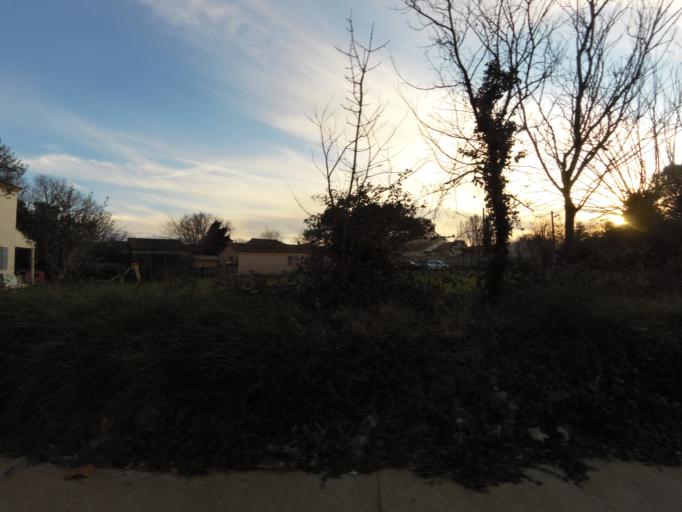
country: FR
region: Languedoc-Roussillon
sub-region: Departement du Gard
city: Saint-Mamert-du-Gard
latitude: 43.8741
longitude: 4.2064
